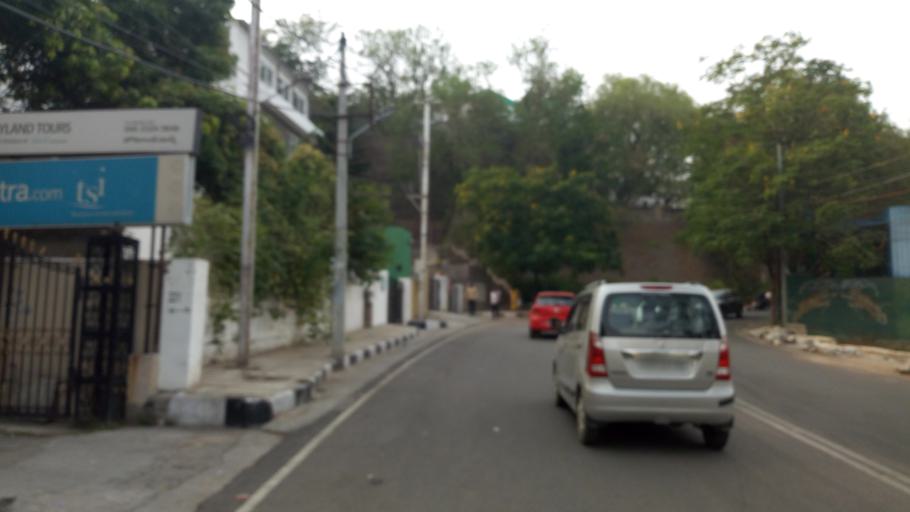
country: IN
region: Telangana
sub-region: Hyderabad
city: Hyderabad
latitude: 17.4028
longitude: 78.4718
